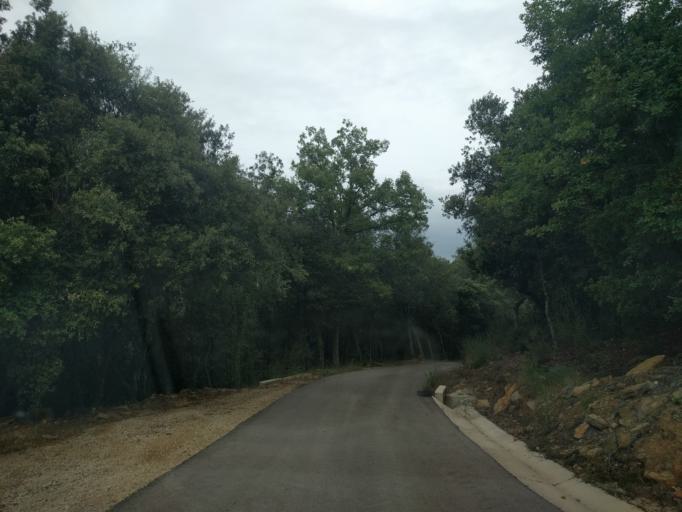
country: ES
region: Catalonia
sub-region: Provincia de Girona
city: la Cellera de Ter
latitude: 42.0257
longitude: 2.6240
